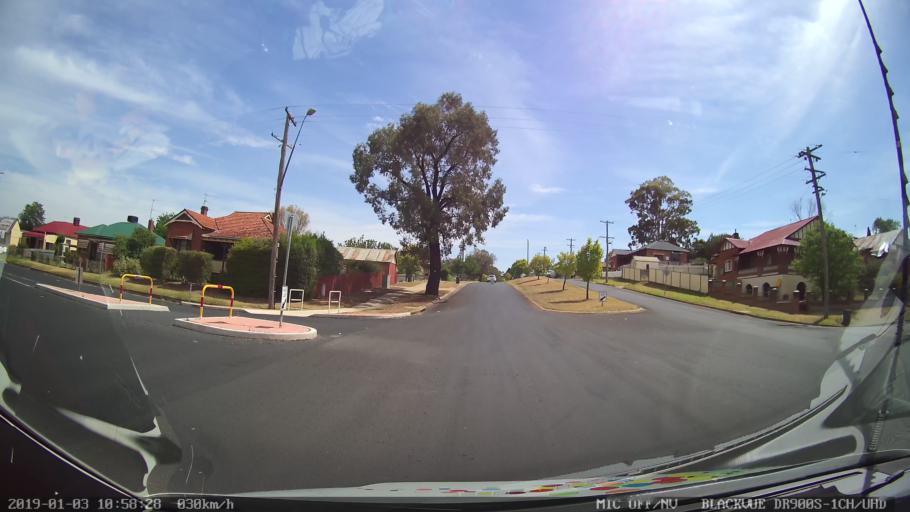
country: AU
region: New South Wales
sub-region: Young
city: Young
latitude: -34.3107
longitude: 148.2962
